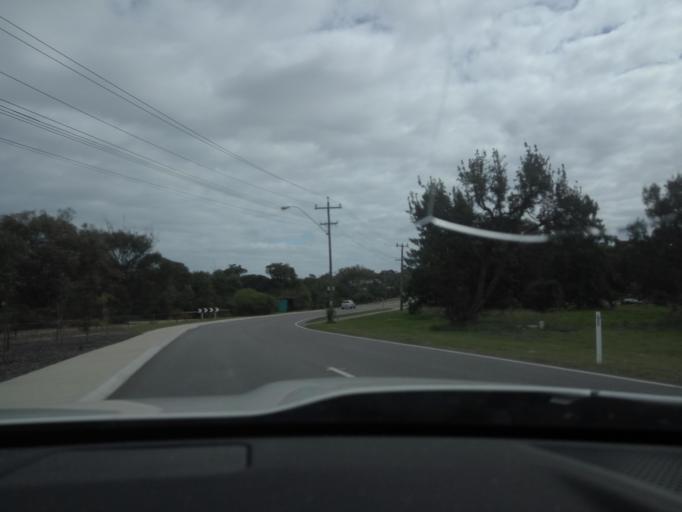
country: AU
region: Western Australia
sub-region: City of Cockburn
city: Bibra Lake
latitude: -32.1016
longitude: 115.8247
